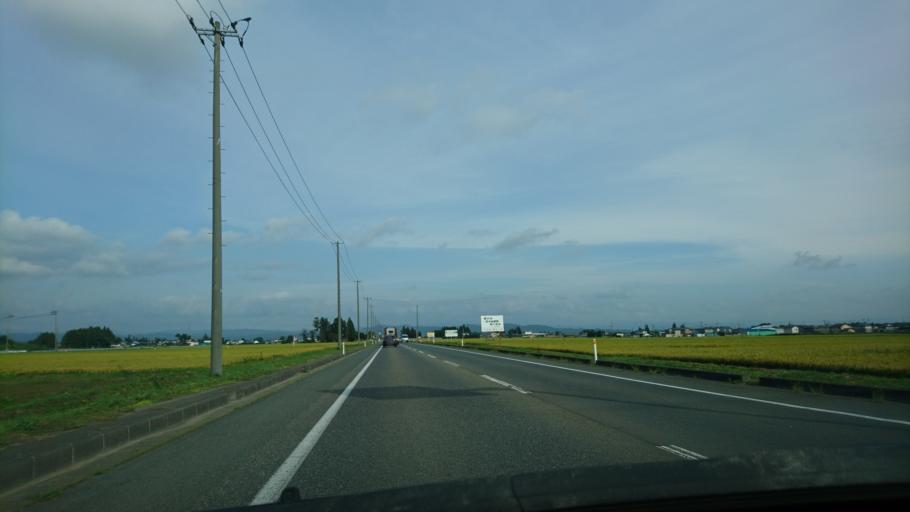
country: JP
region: Iwate
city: Kitakami
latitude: 39.3030
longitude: 141.0448
